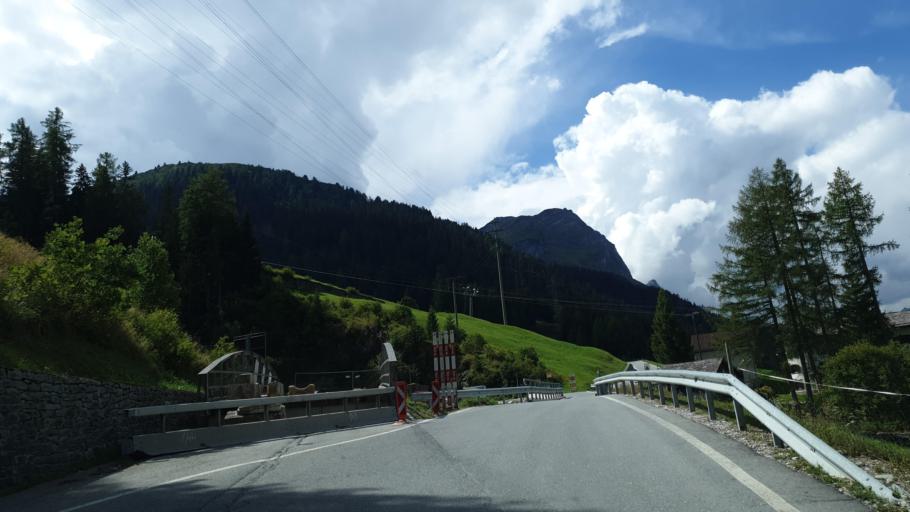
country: CH
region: Grisons
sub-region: Hinterrhein District
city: Hinterrhein
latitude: 46.5481
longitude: 9.3239
